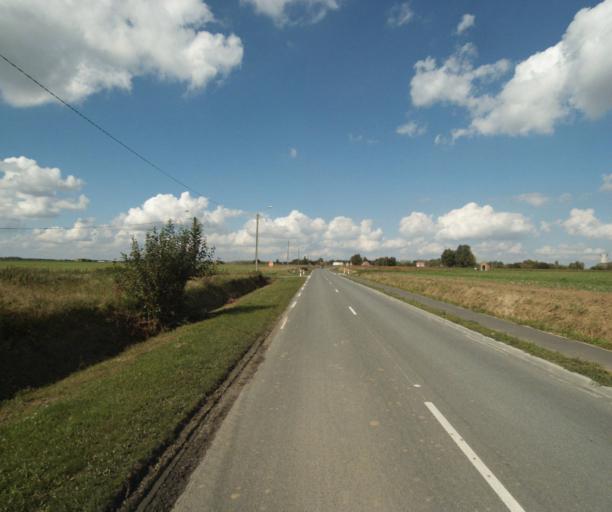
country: FR
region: Nord-Pas-de-Calais
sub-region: Departement du Nord
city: Illies
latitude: 50.5667
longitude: 2.8285
